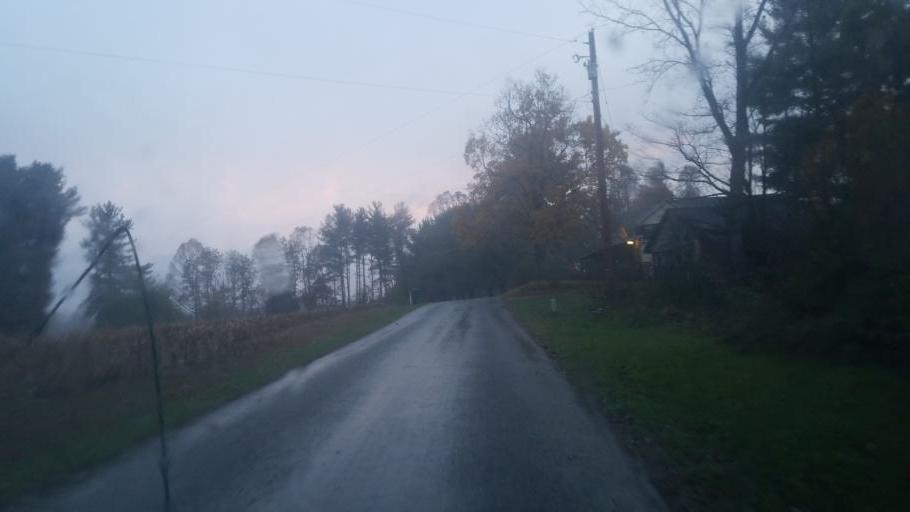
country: US
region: Ohio
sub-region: Morgan County
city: McConnelsville
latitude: 39.5223
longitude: -81.8419
